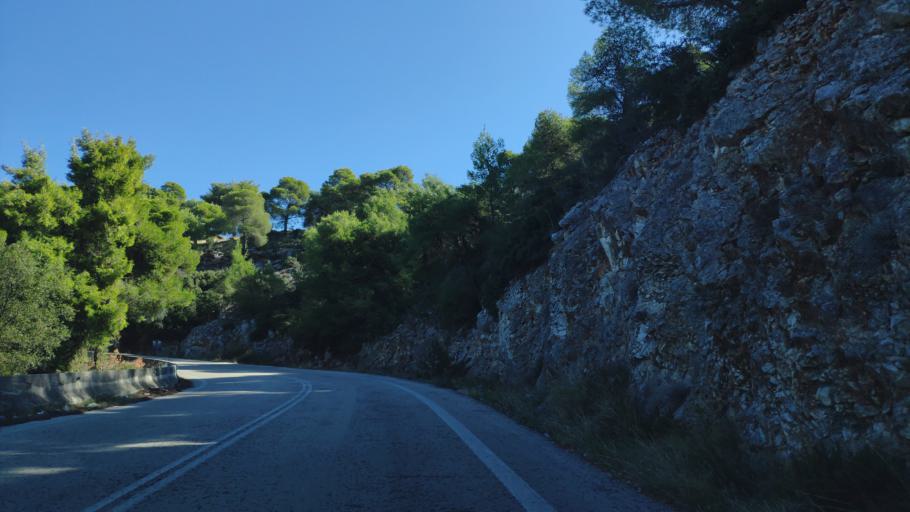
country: GR
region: Peloponnese
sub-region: Nomos Korinthias
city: Sofikon
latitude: 37.8278
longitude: 23.0755
